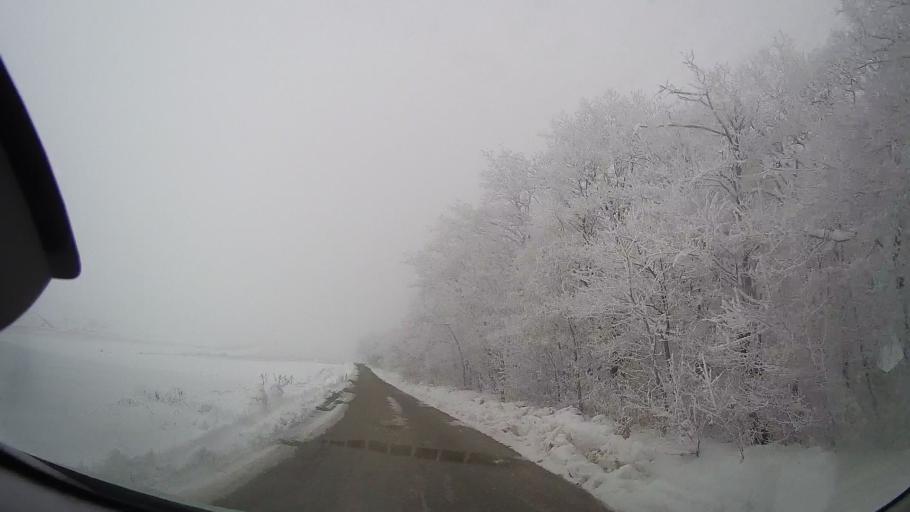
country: RO
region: Iasi
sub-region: Comuna Dagata
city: Dagata
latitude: 46.9132
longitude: 27.1830
